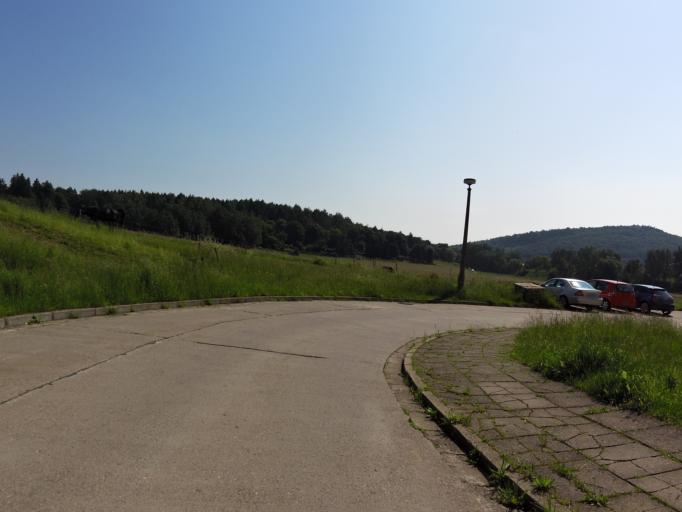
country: DE
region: Thuringia
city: Friedrichroda
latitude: 50.8644
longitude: 10.5765
